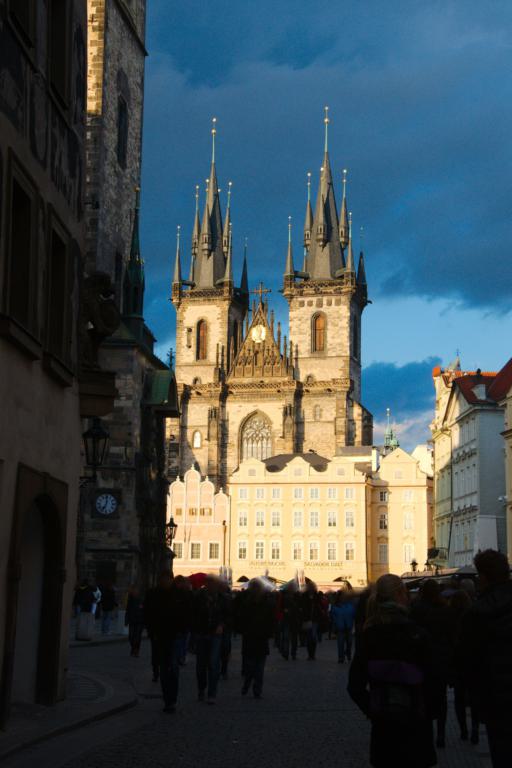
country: CZ
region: Praha
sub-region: Praha 1
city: Stare Mesto
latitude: 50.0867
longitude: 14.4200
